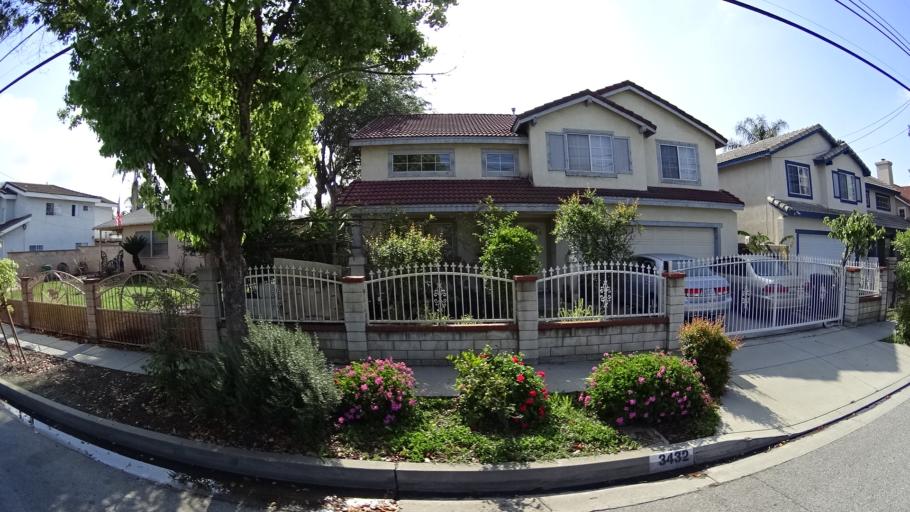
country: US
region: California
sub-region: Los Angeles County
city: Baldwin Park
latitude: 34.0760
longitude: -117.9643
